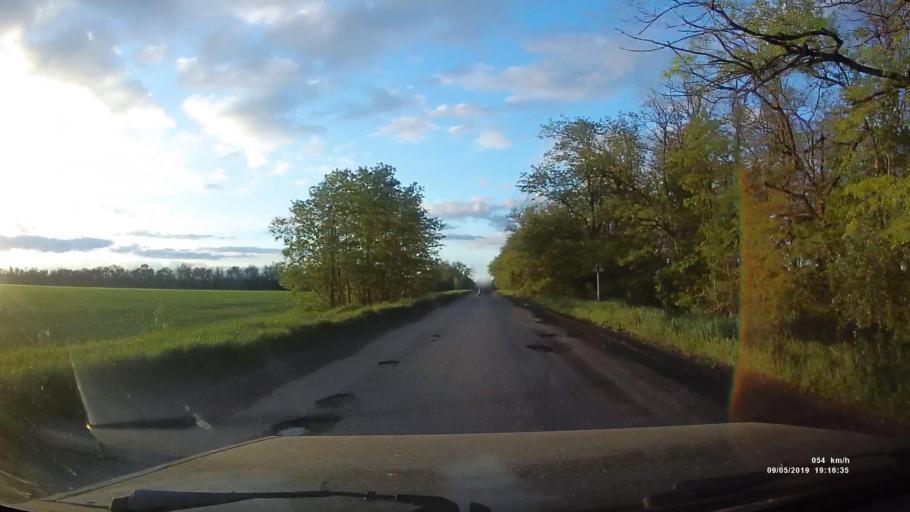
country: RU
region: Krasnodarskiy
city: Kanelovskaya
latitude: 46.7789
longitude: 39.2116
